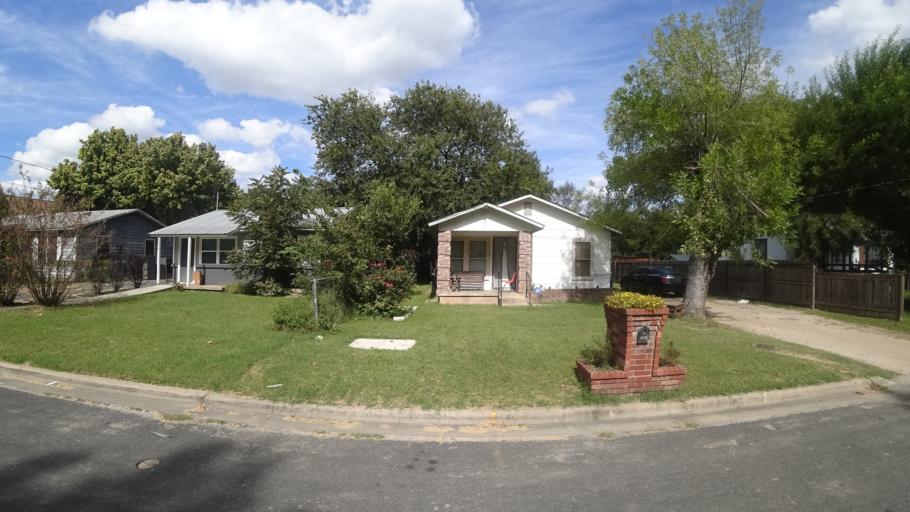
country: US
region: Texas
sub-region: Travis County
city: Austin
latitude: 30.2617
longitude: -97.7079
